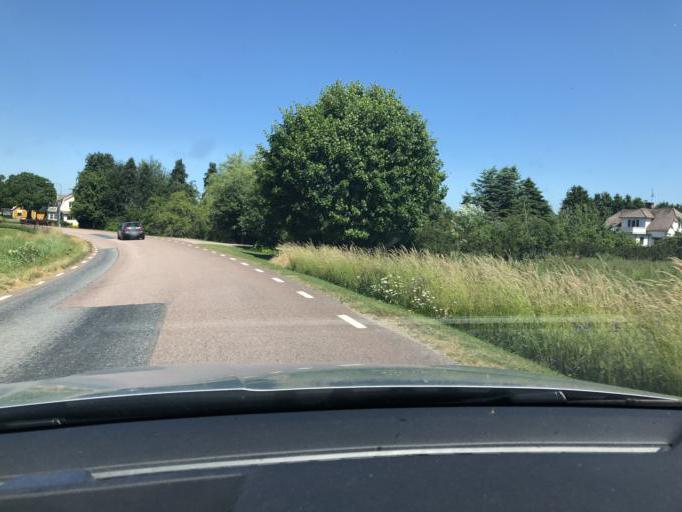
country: SE
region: Blekinge
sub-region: Olofstroms Kommun
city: Jamshog
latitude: 56.1792
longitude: 14.6126
